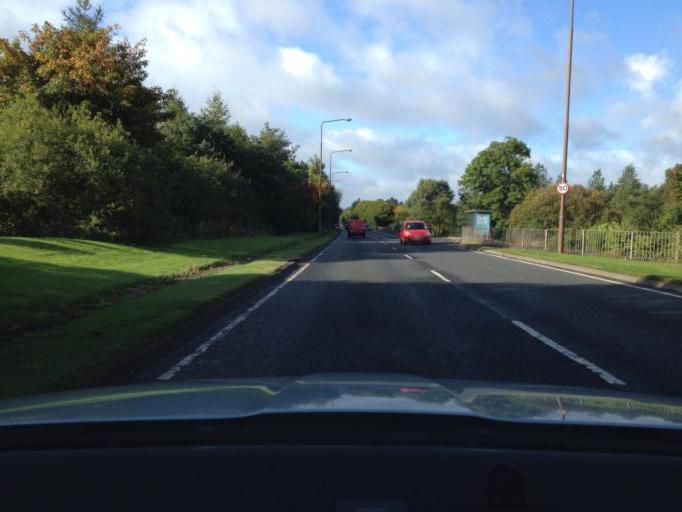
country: GB
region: Scotland
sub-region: West Lothian
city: Livingston
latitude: 55.8704
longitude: -3.5277
